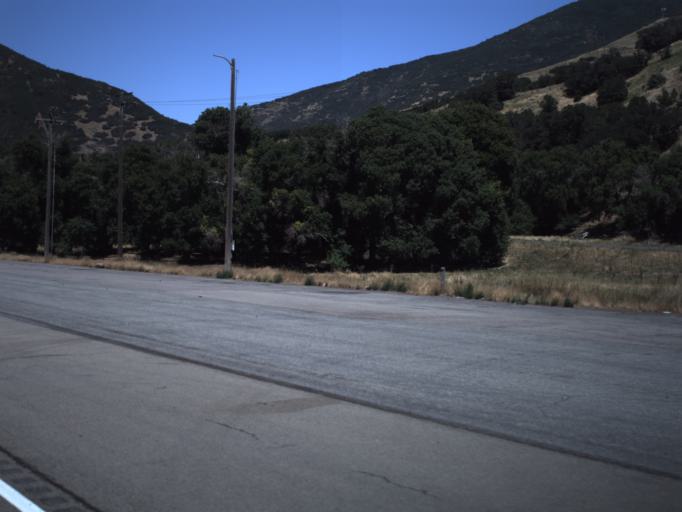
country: US
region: Utah
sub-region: Utah County
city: Mapleton
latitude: 40.0415
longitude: -111.5429
